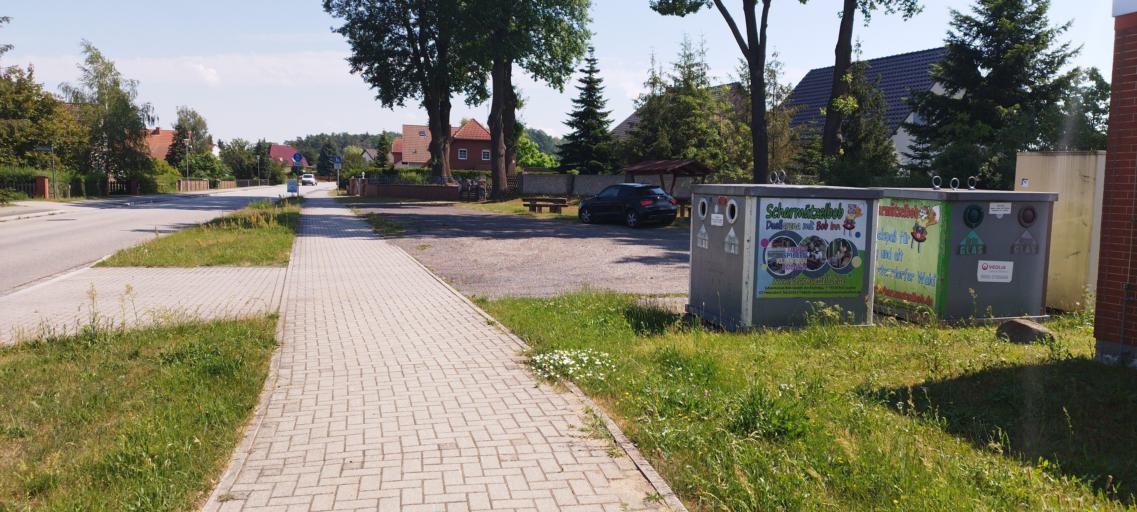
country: DE
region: Brandenburg
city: Bad Saarow
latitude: 52.3023
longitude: 14.0862
